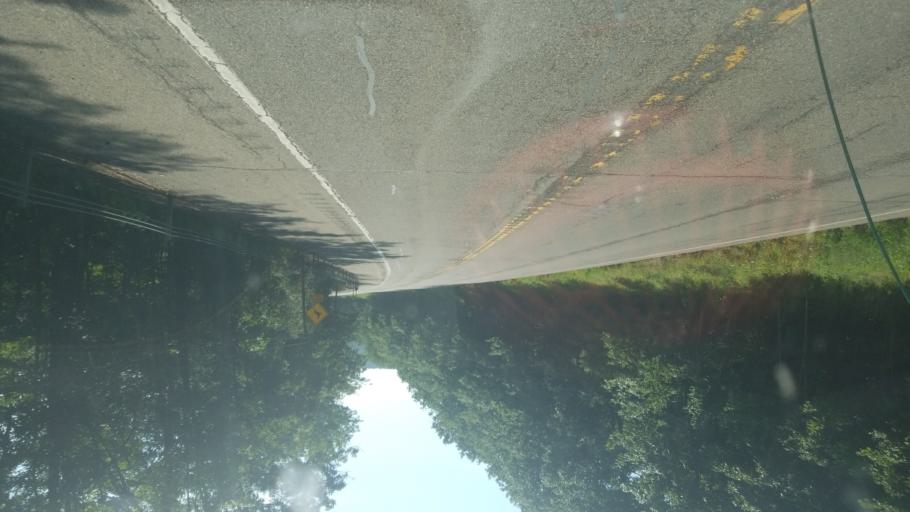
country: US
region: New York
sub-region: Allegany County
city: Wellsville
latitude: 42.1071
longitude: -78.0212
